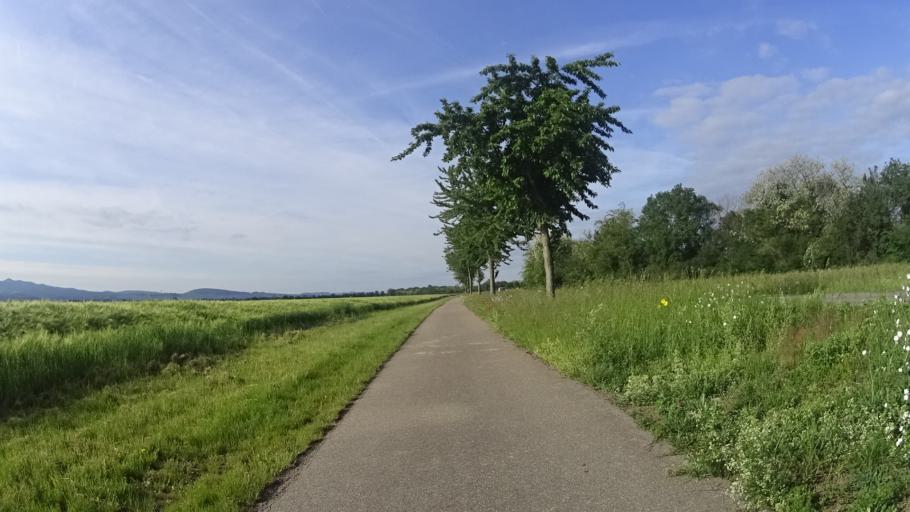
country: FR
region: Alsace
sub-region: Departement du Haut-Rhin
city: Blodelsheim
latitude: 47.8625
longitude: 7.5860
